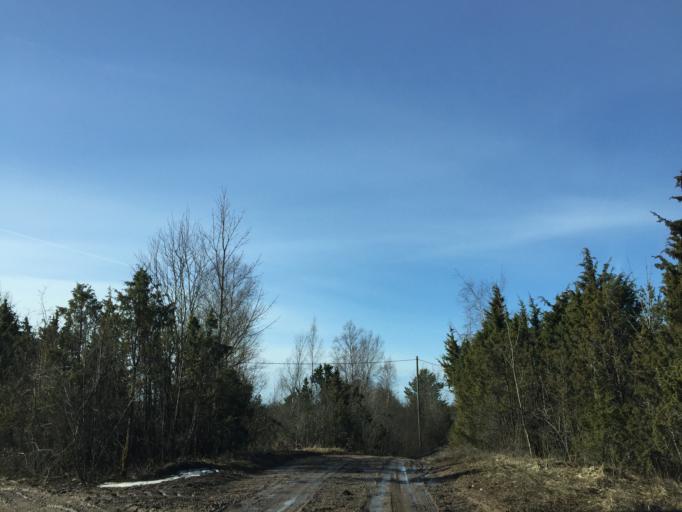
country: EE
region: Laeaene
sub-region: Haapsalu linn
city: Haapsalu
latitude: 58.6614
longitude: 23.5185
